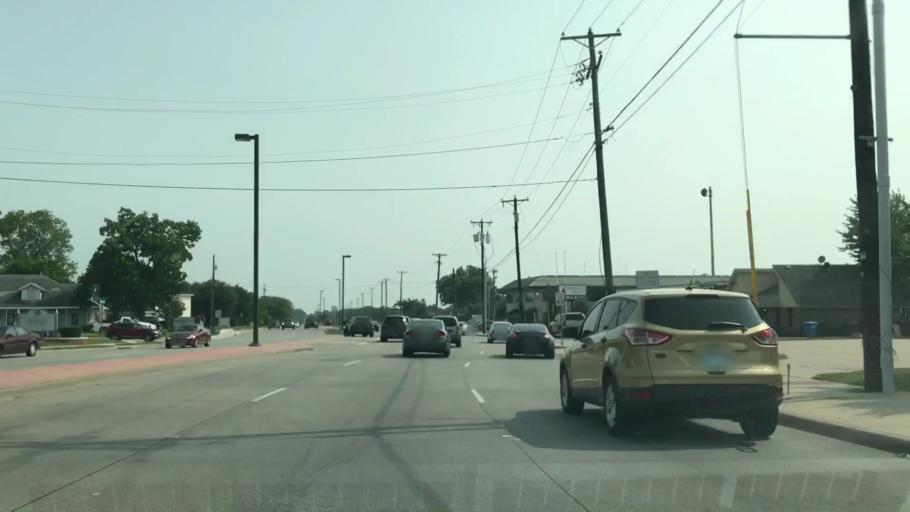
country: US
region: Texas
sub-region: Dallas County
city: Rowlett
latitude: 32.9024
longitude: -96.5695
